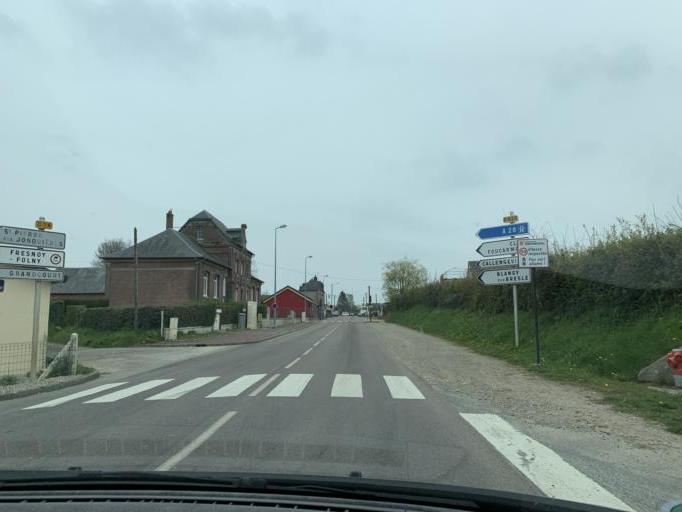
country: FR
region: Haute-Normandie
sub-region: Departement de la Seine-Maritime
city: Londinieres
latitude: 49.8421
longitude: 1.4756
